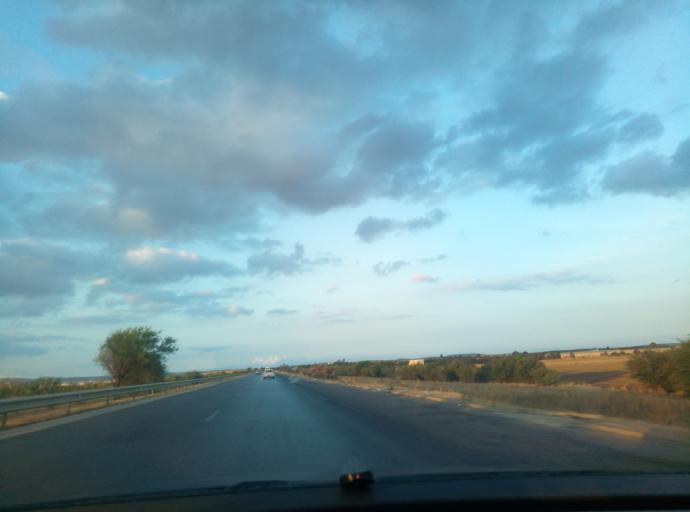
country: TN
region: Tunis
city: Oued Lill
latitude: 36.7159
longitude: 9.9778
